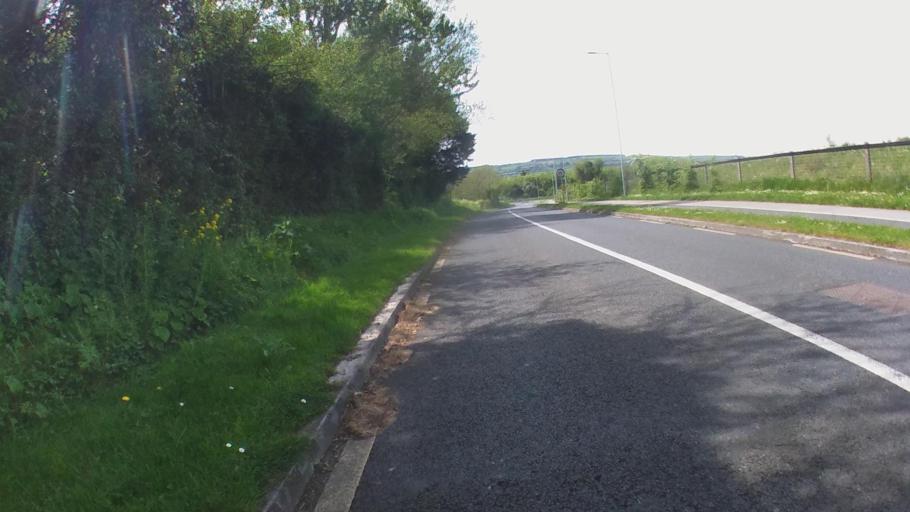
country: IE
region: Leinster
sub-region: County Carlow
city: Carlow
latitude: 52.8334
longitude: -6.9507
